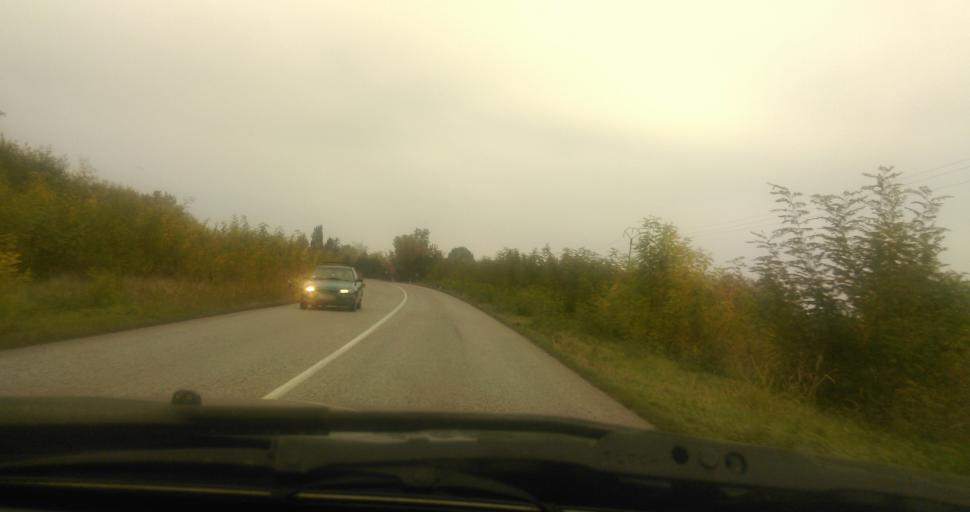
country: RS
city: Backo Gradiste
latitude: 45.5699
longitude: 20.0203
